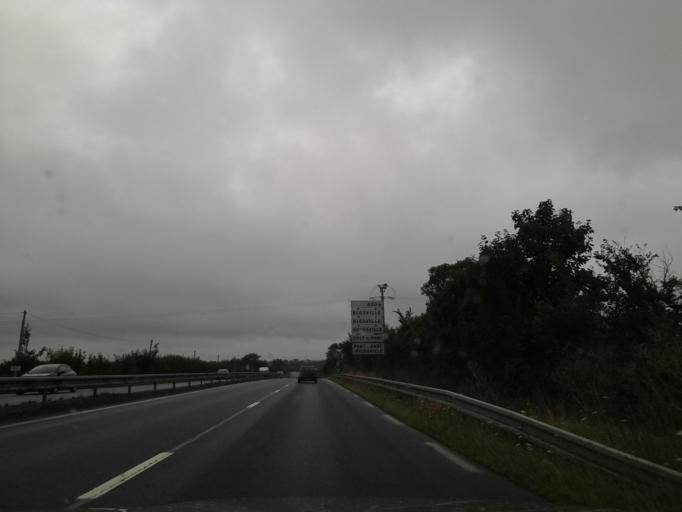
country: FR
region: Lower Normandy
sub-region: Departement de la Manche
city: Carentan
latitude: 49.3525
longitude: -1.2770
